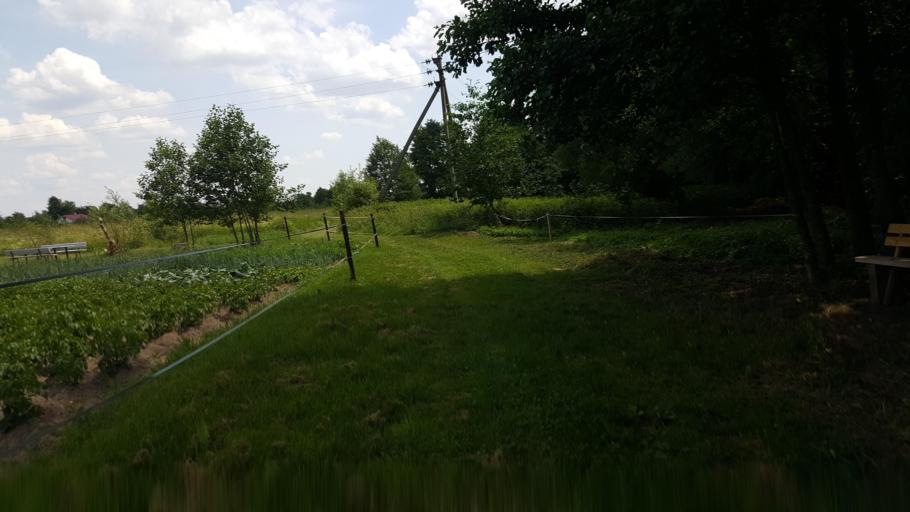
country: BY
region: Brest
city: Kamyanyets
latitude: 52.4048
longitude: 23.7845
